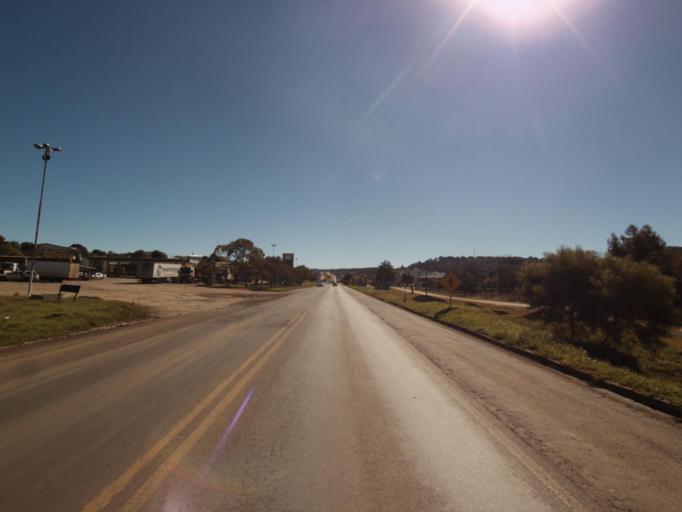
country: BR
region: Santa Catarina
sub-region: Concordia
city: Concordia
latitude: -26.8769
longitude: -52.0158
